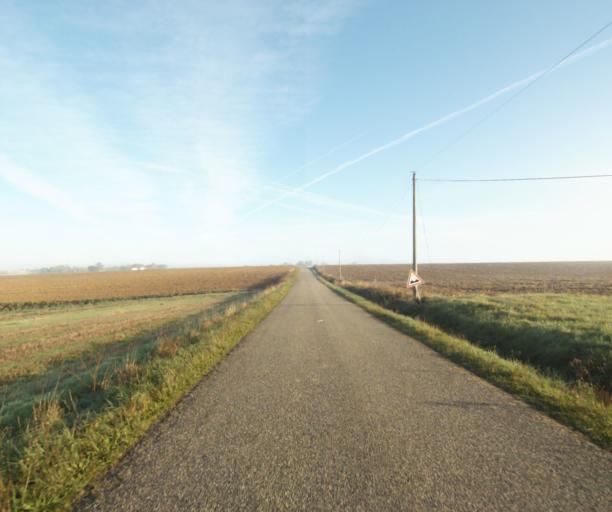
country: FR
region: Midi-Pyrenees
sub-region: Departement de la Haute-Garonne
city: Villemur-sur-Tarn
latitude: 43.9121
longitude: 1.4932
